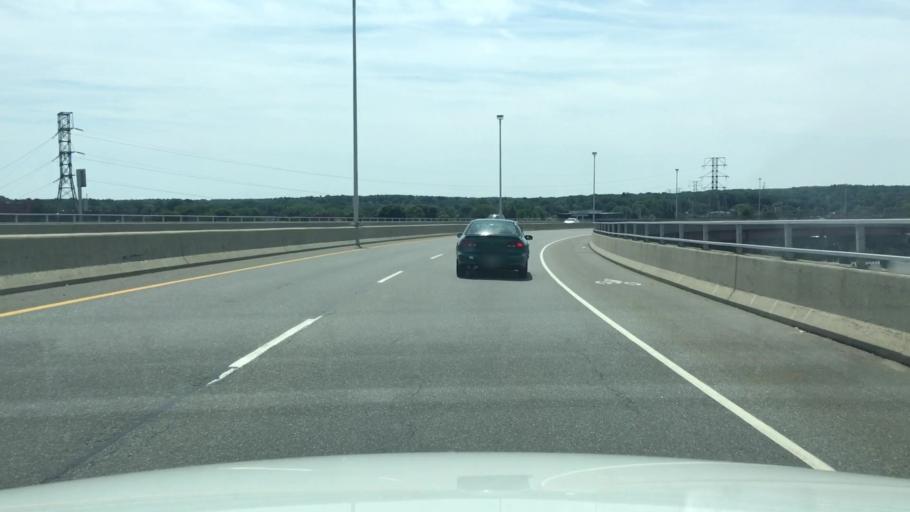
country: US
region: Maine
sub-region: Cumberland County
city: South Portland
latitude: 43.6431
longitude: -70.2568
